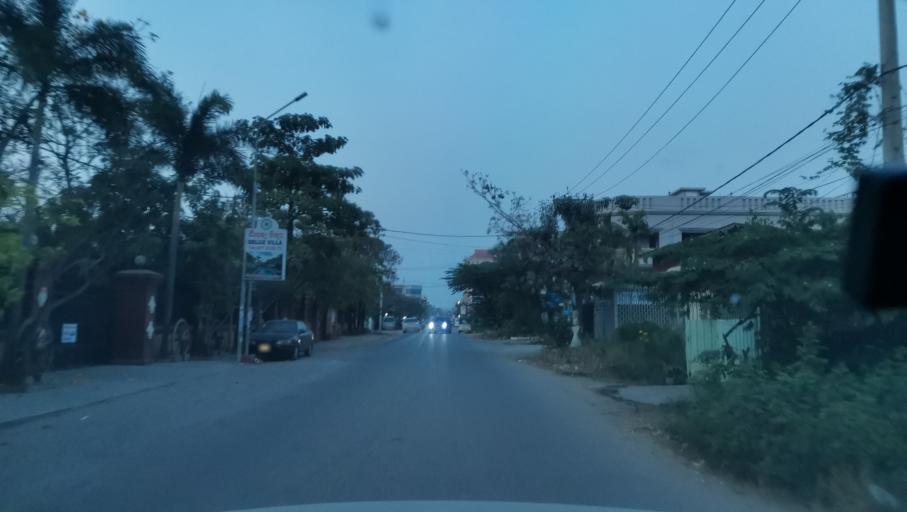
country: KH
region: Battambang
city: Battambang
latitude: 13.1006
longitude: 103.1952
